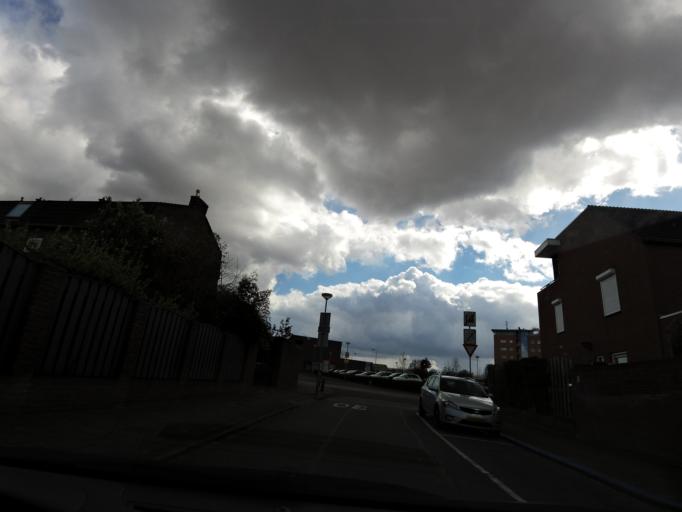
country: NL
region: Limburg
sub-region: Gemeente Heerlen
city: Heerlen
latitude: 50.9065
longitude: 6.0225
